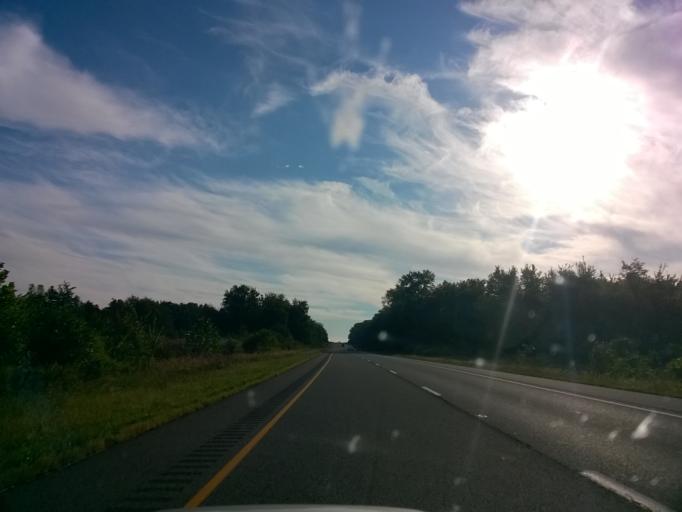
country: US
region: Indiana
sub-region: Spencer County
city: Dale
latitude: 38.1970
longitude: -87.1320
